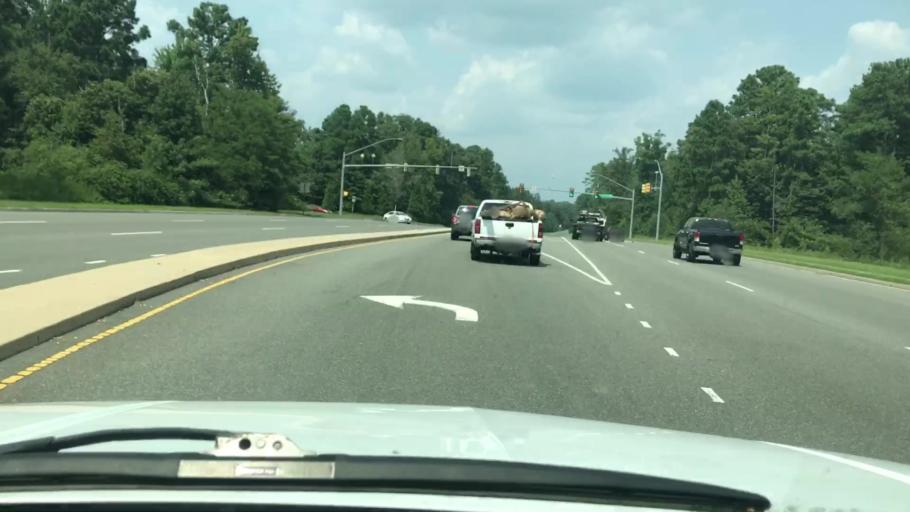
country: US
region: Virginia
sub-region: Henrico County
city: Short Pump
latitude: 37.6345
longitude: -77.6133
